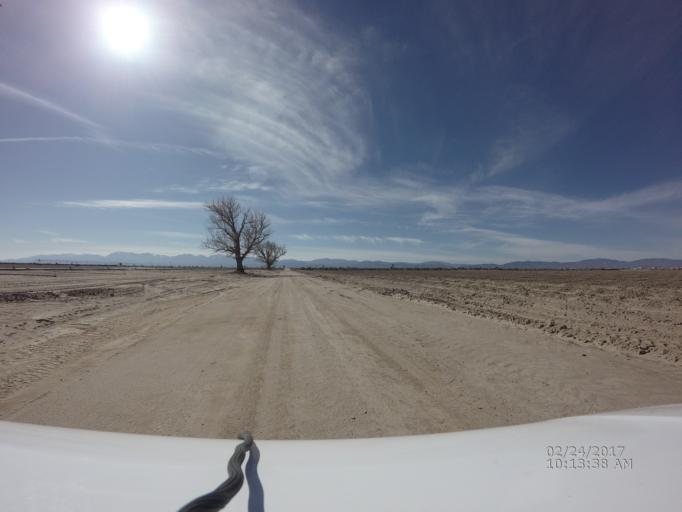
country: US
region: California
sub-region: Los Angeles County
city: Littlerock
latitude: 34.6662
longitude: -117.9874
